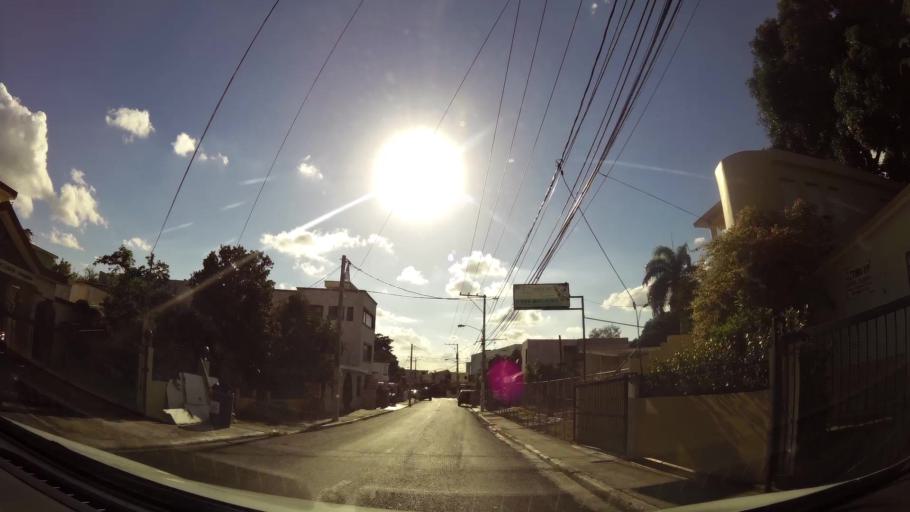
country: DO
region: Santiago
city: Santiago de los Caballeros
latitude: 19.4647
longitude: -70.6899
